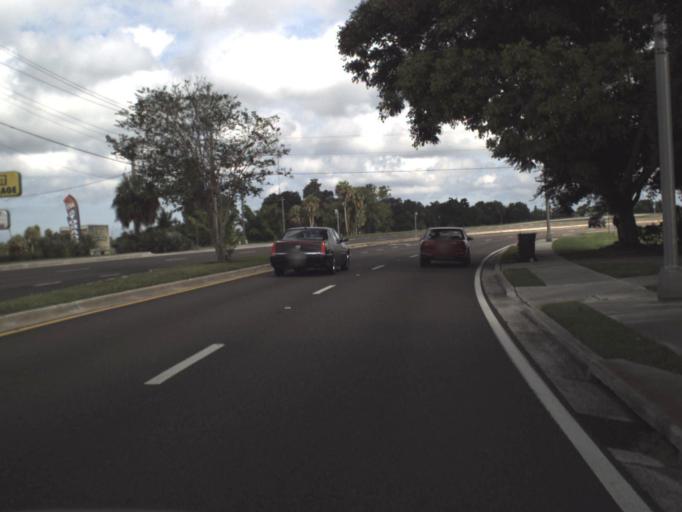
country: US
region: Florida
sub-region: Manatee County
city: Palmetto
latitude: 27.5315
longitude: -82.5728
